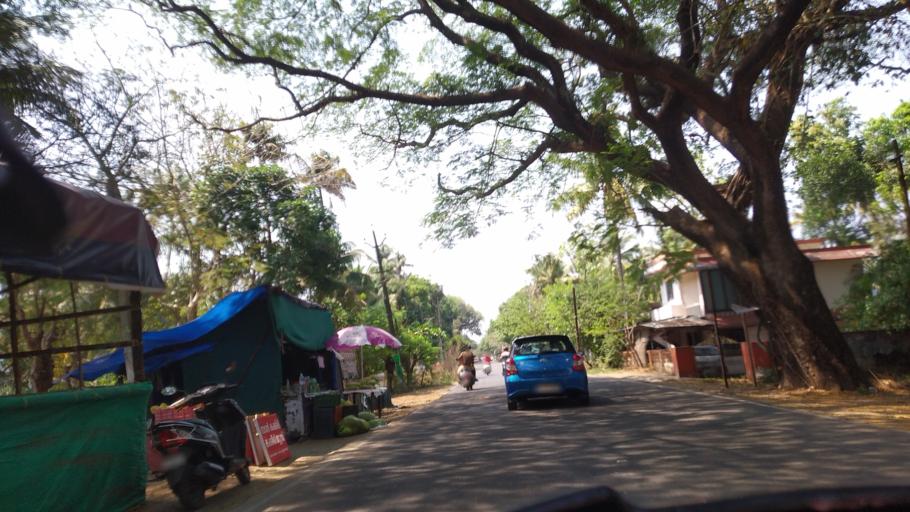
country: IN
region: Kerala
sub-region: Thrissur District
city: Kodungallur
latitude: 10.2178
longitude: 76.1600
